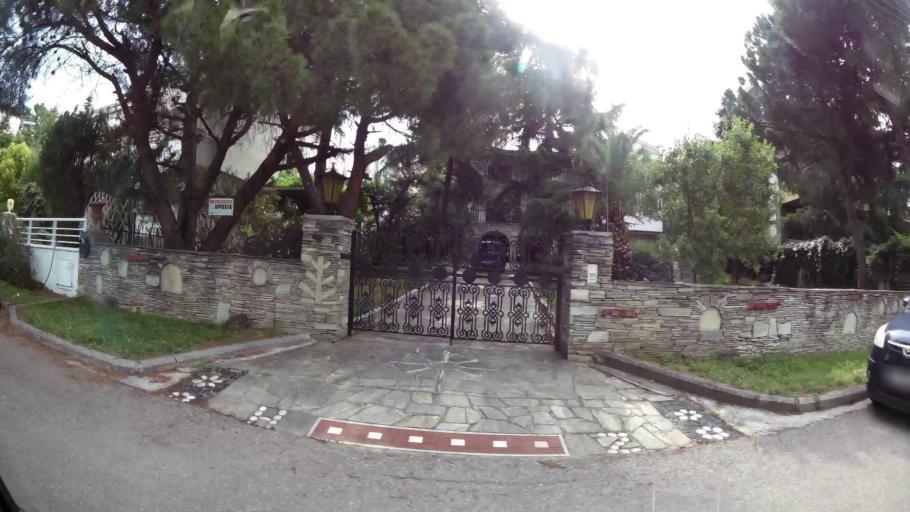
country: GR
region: Central Macedonia
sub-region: Nomos Thessalonikis
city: Panorama
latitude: 40.5834
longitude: 23.0283
